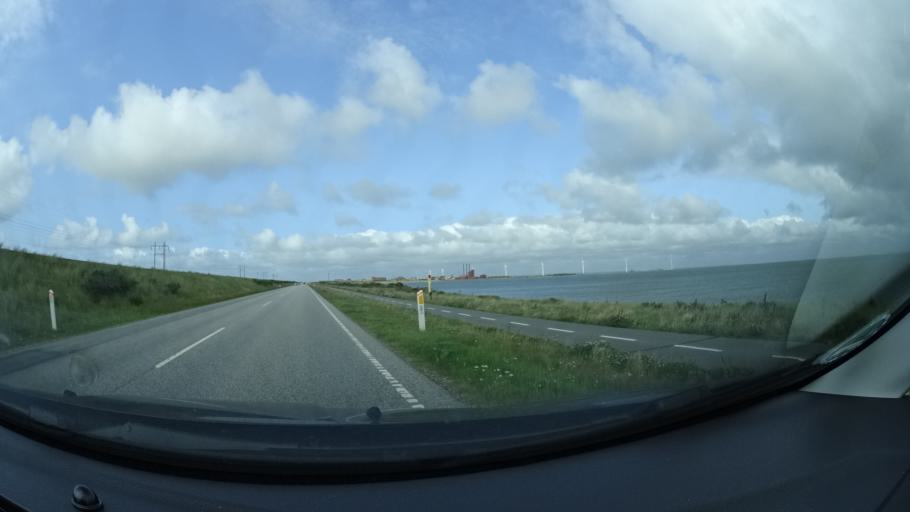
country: DK
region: Central Jutland
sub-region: Lemvig Kommune
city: Harboore
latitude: 56.6434
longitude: 8.1894
